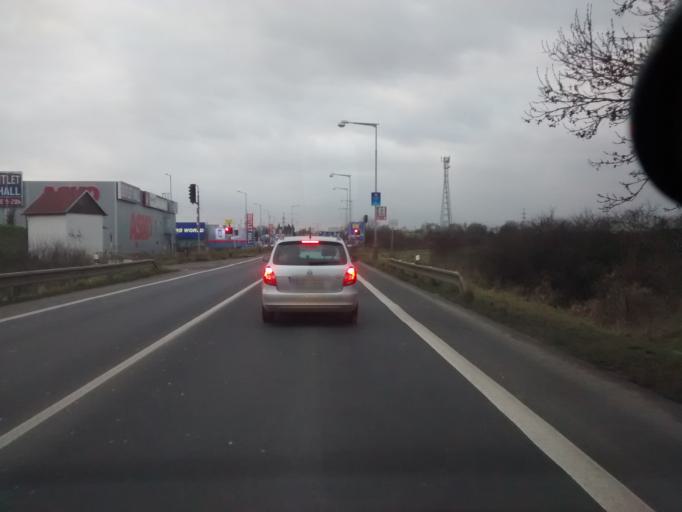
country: CZ
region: Central Bohemia
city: Kosmonosy
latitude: 50.4092
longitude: 14.9483
